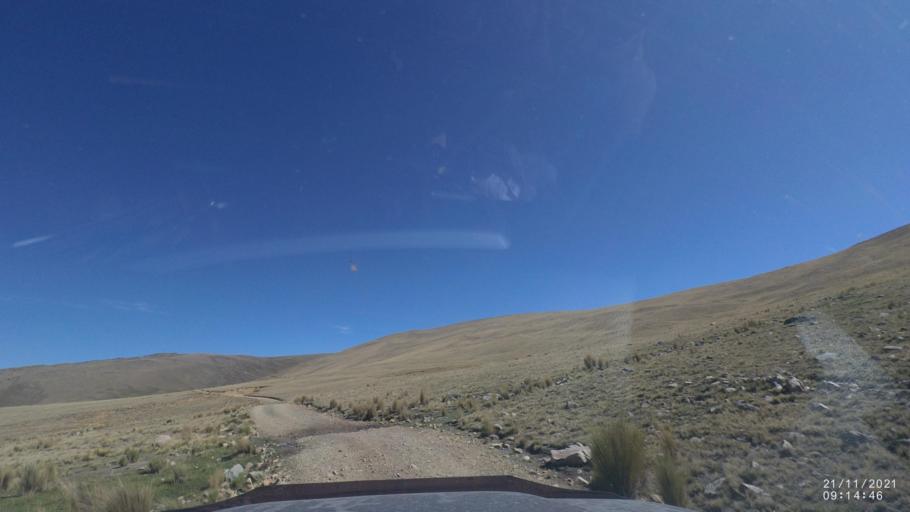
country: BO
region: Cochabamba
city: Cochabamba
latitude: -17.1337
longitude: -66.2562
